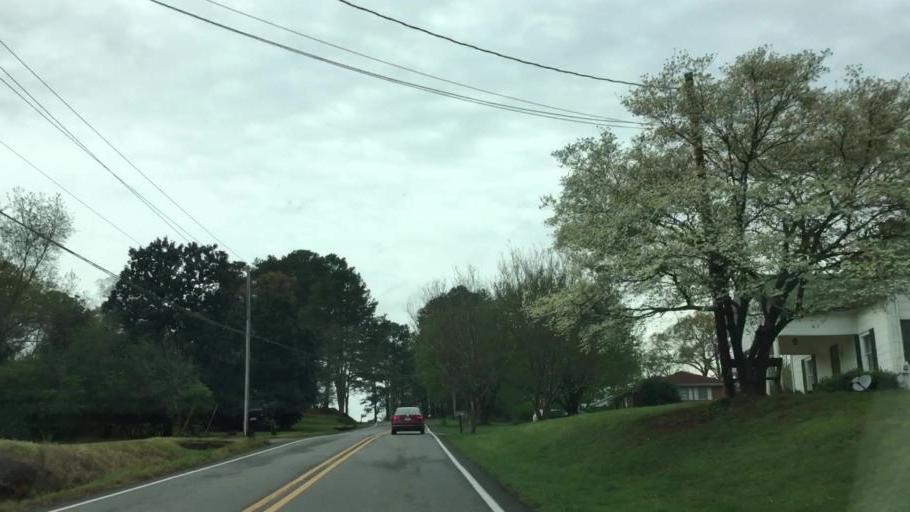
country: US
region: Georgia
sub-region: Cherokee County
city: Canton
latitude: 34.2087
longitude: -84.3944
